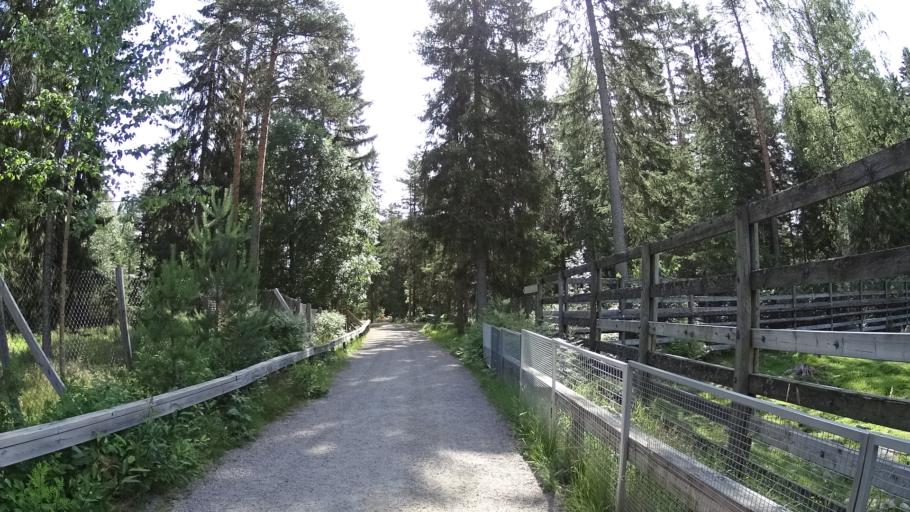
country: FI
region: Southern Ostrobothnia
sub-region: Kuusiokunnat
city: AEhtaeri
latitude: 62.5401
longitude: 24.1816
